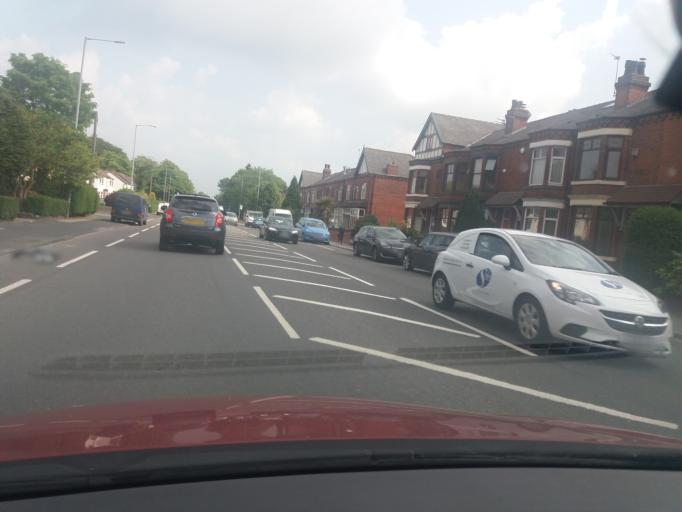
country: GB
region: England
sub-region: Borough of Bolton
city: Horwich
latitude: 53.5883
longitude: -2.5312
